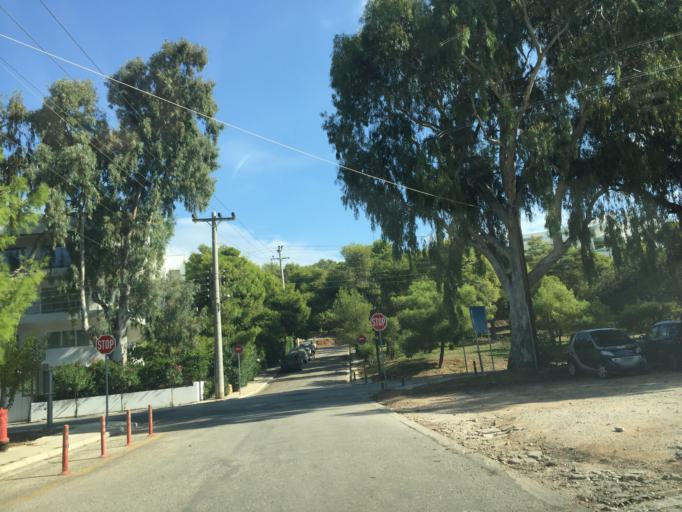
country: GR
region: Attica
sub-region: Nomarchia Anatolikis Attikis
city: Vouliagmeni
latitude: 37.8174
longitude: 23.7714
